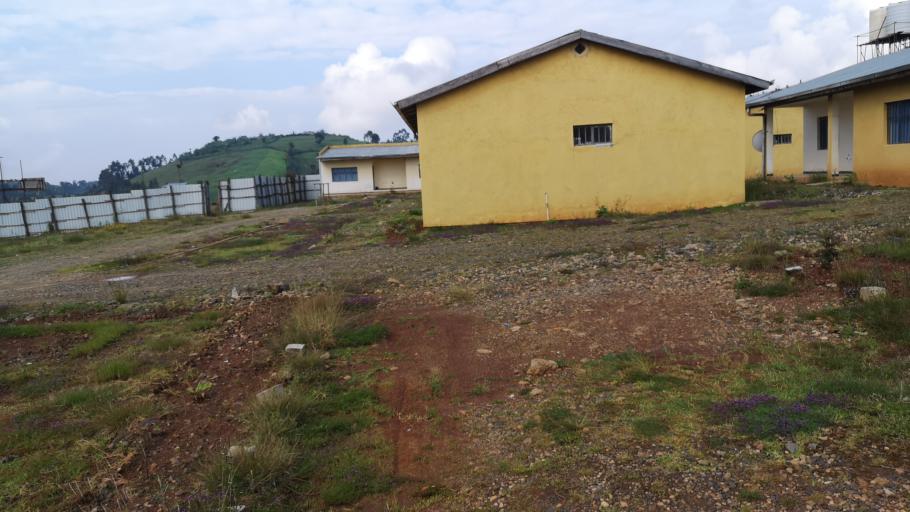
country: ET
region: Southern Nations, Nationalities, and People's Region
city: Hagere Selam
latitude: 6.4985
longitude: 38.9544
